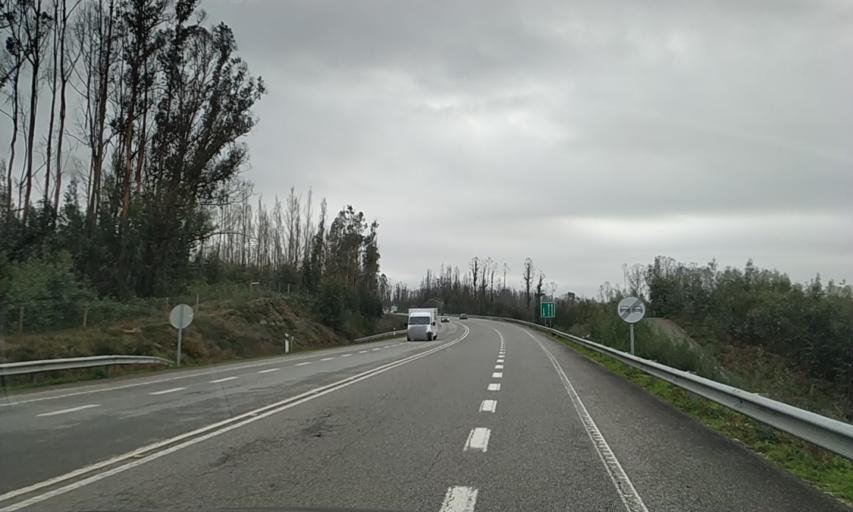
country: PT
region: Viseu
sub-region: Santa Comba Dao
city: Santa Comba Dao
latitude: 40.4514
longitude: -8.1055
